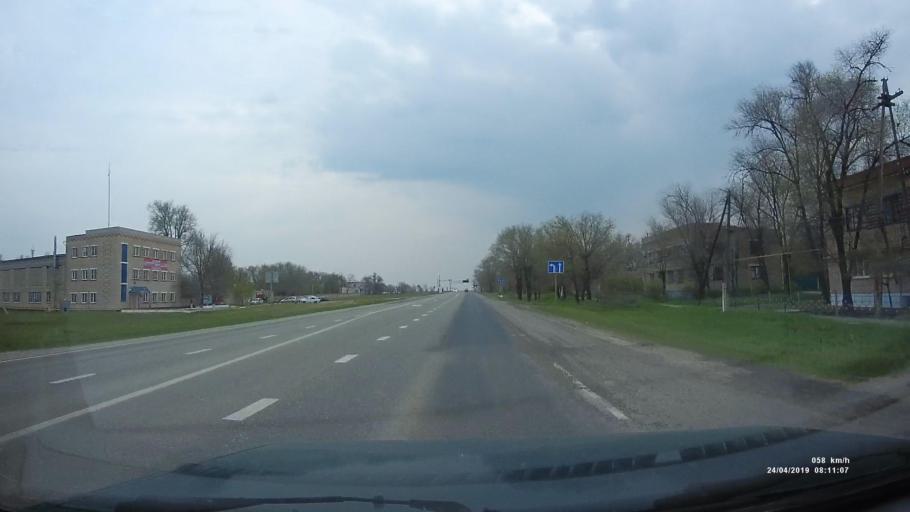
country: RU
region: Kalmykiya
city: Priyutnoye
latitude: 46.1008
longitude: 43.5245
